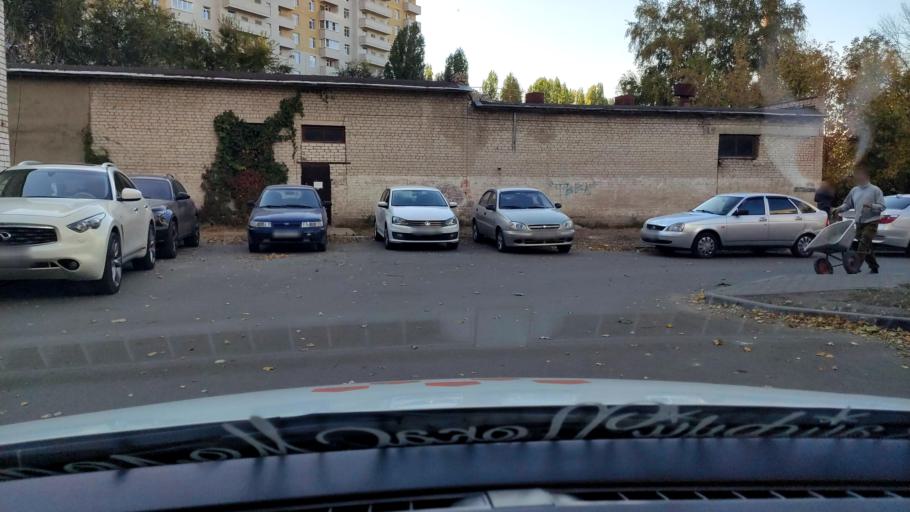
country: RU
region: Voronezj
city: Voronezh
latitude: 51.6362
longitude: 39.1843
